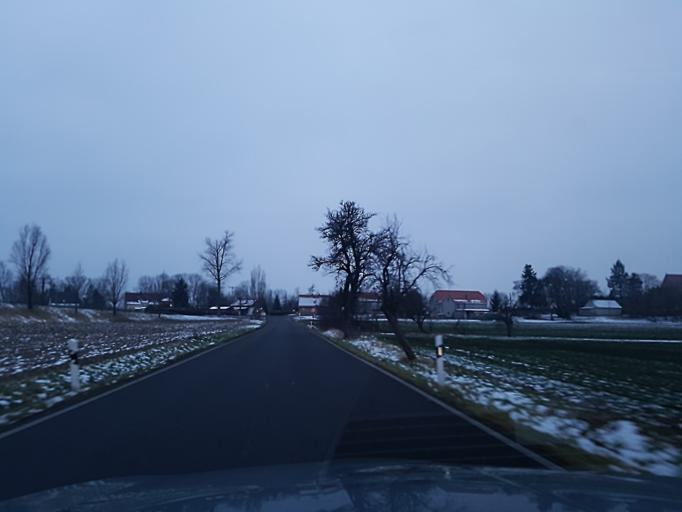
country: DE
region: Saxony
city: Stauchitz
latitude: 51.2624
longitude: 13.2243
